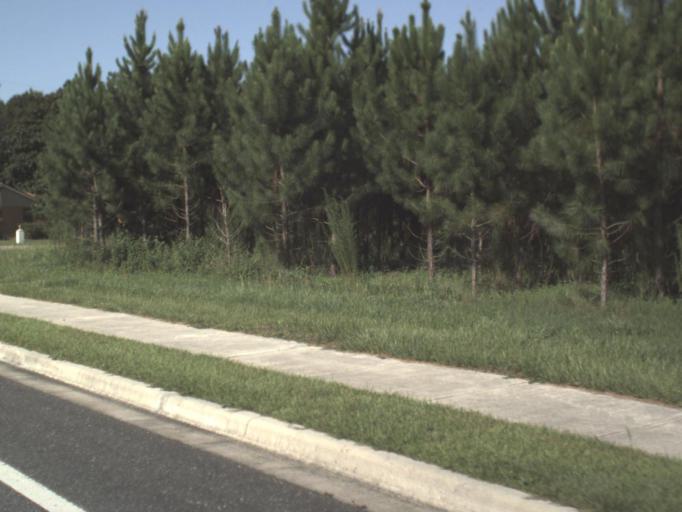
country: US
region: Florida
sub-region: Columbia County
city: Lake City
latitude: 30.1353
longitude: -82.6515
